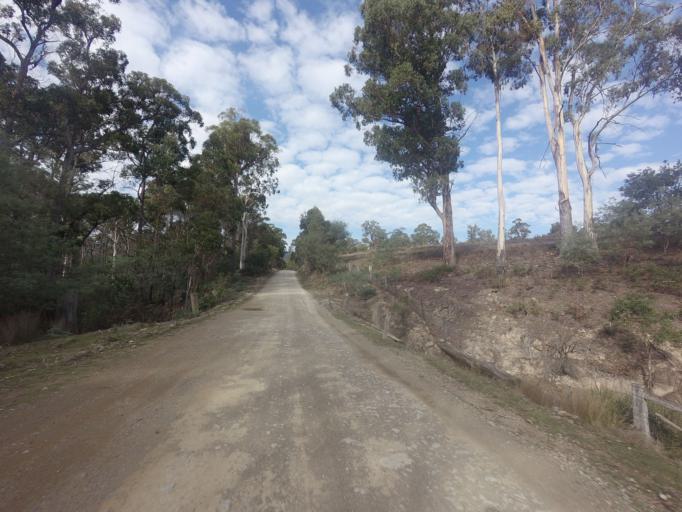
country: AU
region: Tasmania
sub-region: Sorell
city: Sorell
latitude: -42.5646
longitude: 147.4693
